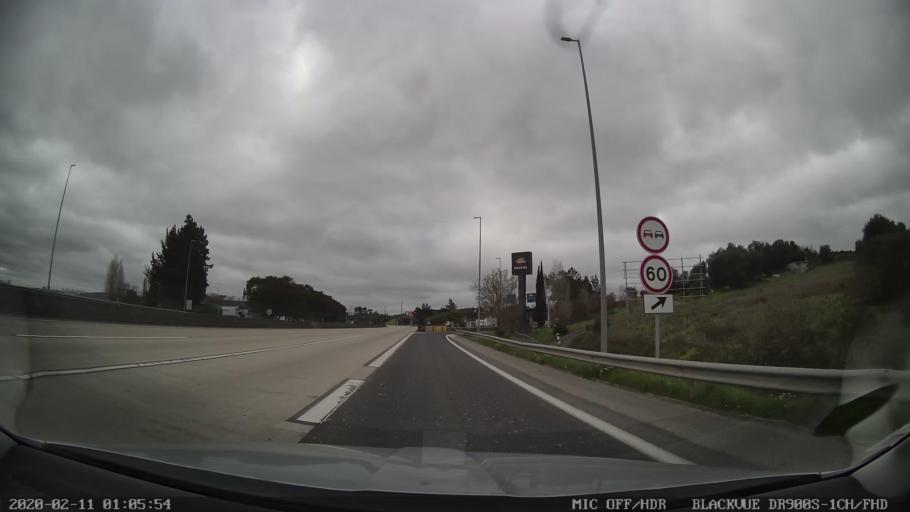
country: PT
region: Lisbon
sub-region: Loures
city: Santo Antao do Tojal
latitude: 38.8598
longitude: -9.1596
